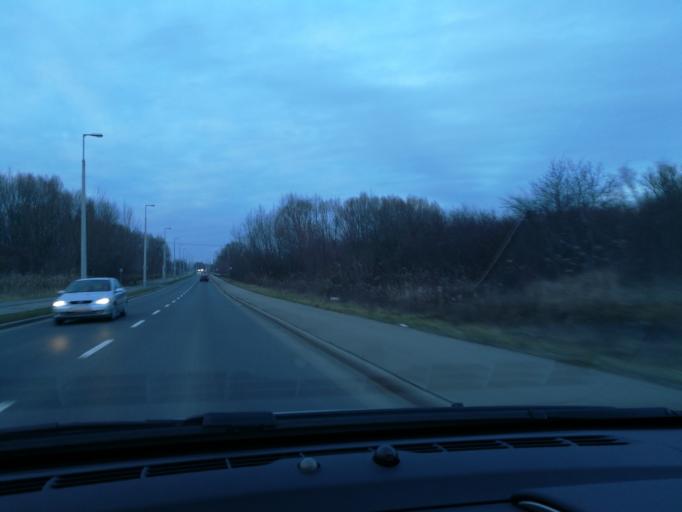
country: HU
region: Szabolcs-Szatmar-Bereg
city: Nyiregyhaza
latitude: 47.9647
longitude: 21.7431
